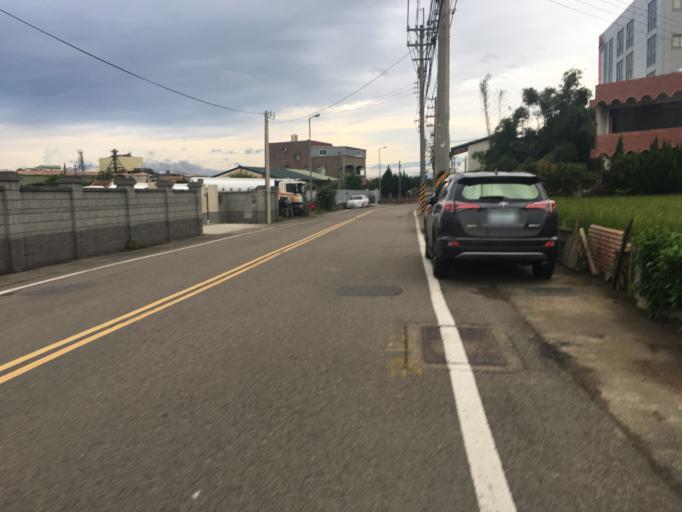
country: TW
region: Taiwan
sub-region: Hsinchu
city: Hsinchu
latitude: 24.7293
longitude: 120.9107
